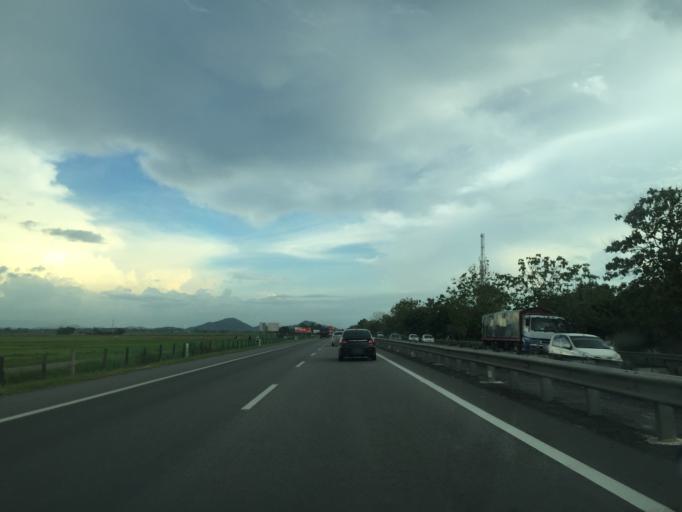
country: MY
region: Kedah
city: Alor Setar
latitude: 5.9945
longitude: 100.4286
